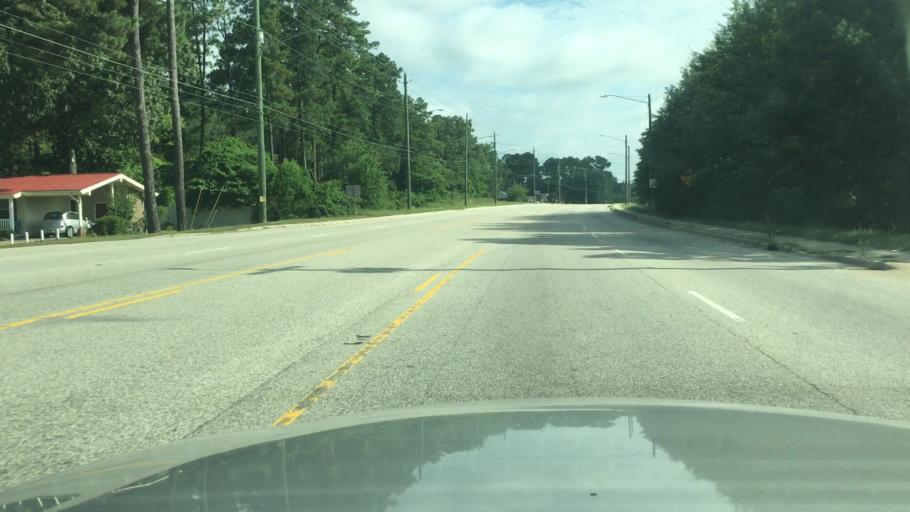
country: US
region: North Carolina
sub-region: Cumberland County
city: Hope Mills
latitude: 35.0082
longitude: -78.9669
